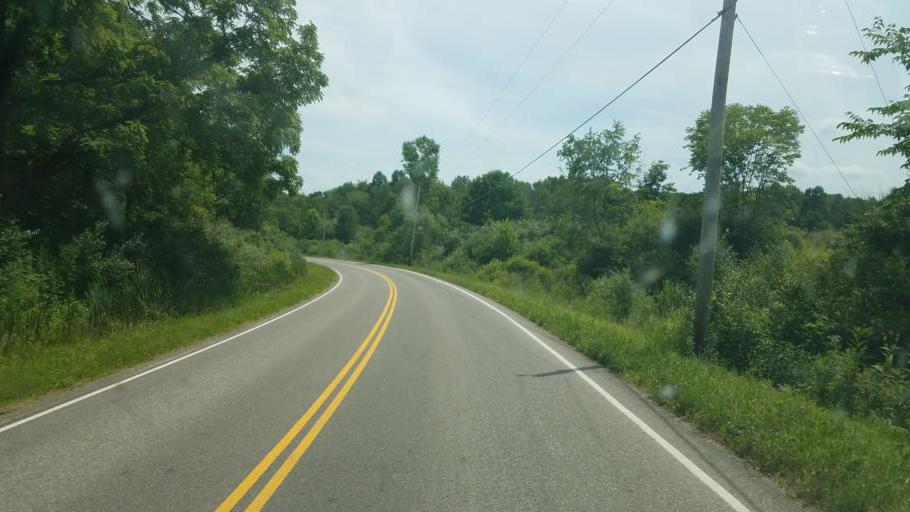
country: US
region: Ohio
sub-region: Knox County
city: Fredericktown
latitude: 40.5100
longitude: -82.5921
